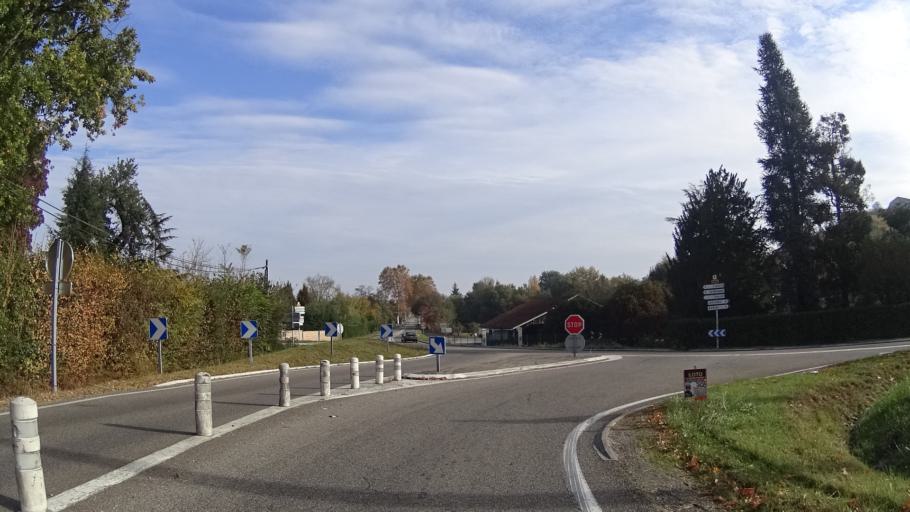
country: FR
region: Aquitaine
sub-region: Departement du Lot-et-Garonne
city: Roquefort
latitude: 44.1711
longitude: 0.5517
